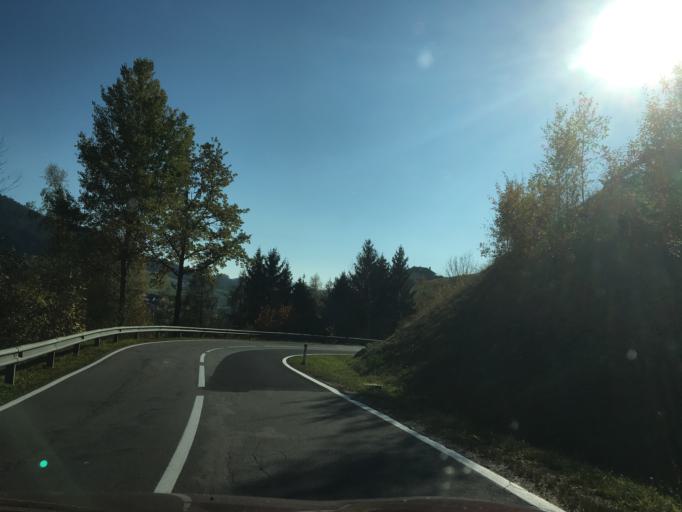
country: AT
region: Upper Austria
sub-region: Politischer Bezirk Perg
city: Sankt Georgen am Walde
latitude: 48.4411
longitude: 14.7799
